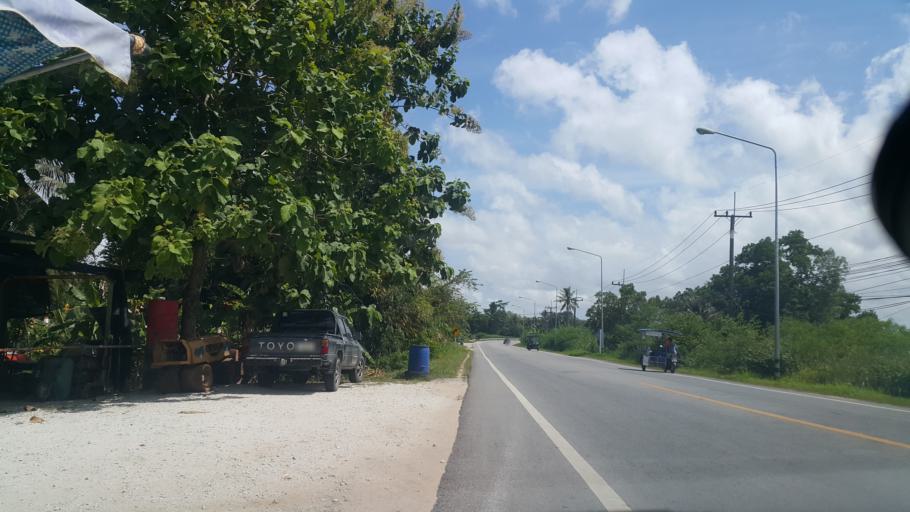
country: TH
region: Rayong
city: Ban Chang
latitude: 12.7896
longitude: 101.0301
